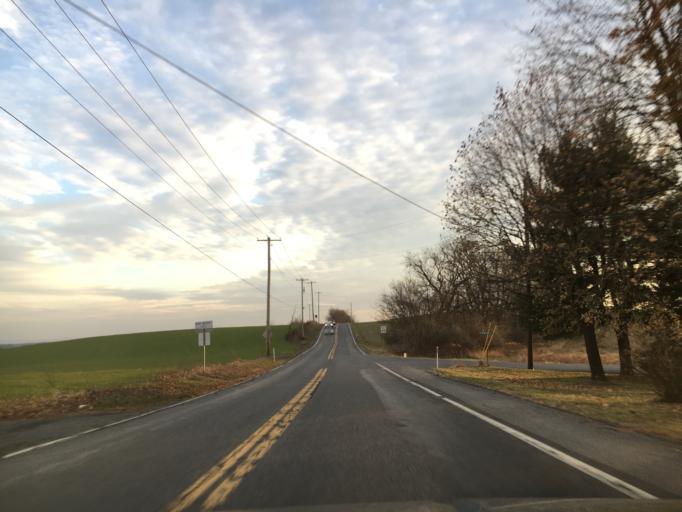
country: US
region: Pennsylvania
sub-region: Lehigh County
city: Slatington
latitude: 40.7136
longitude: -75.5963
